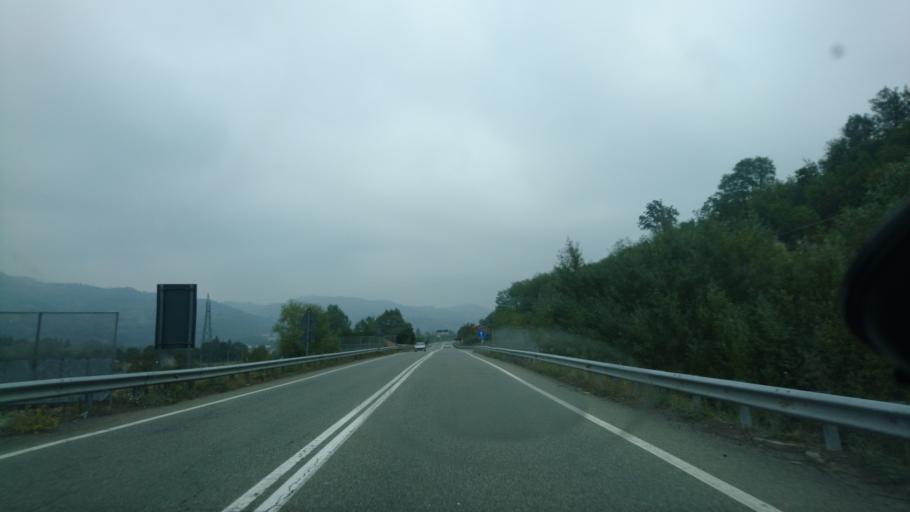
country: IT
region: Piedmont
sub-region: Provincia di Alessandria
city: Ponti
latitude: 44.6449
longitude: 8.3571
